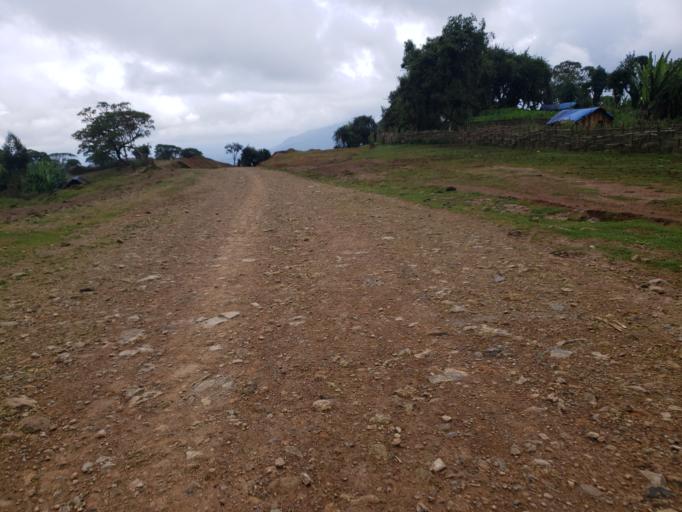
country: ET
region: Oromiya
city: Dodola
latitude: 6.6897
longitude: 39.3697
